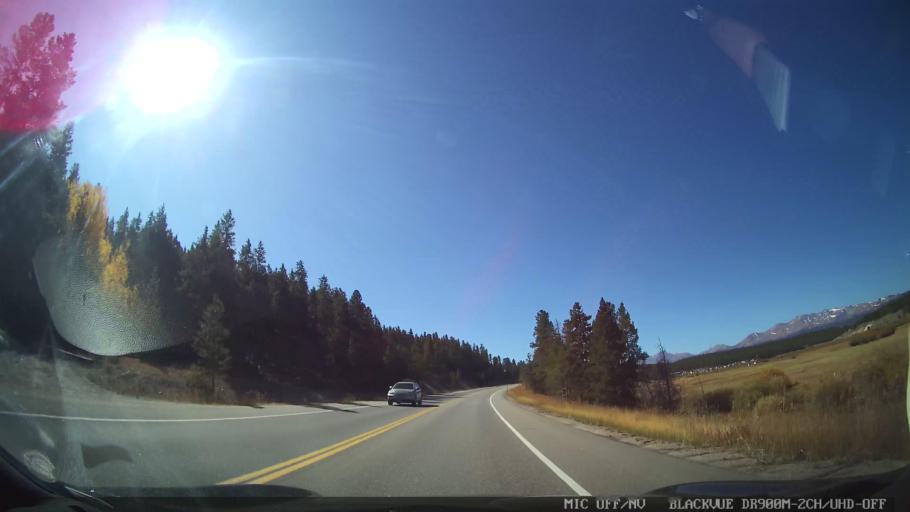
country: US
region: Colorado
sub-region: Lake County
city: Leadville North
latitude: 39.2819
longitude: -106.2805
